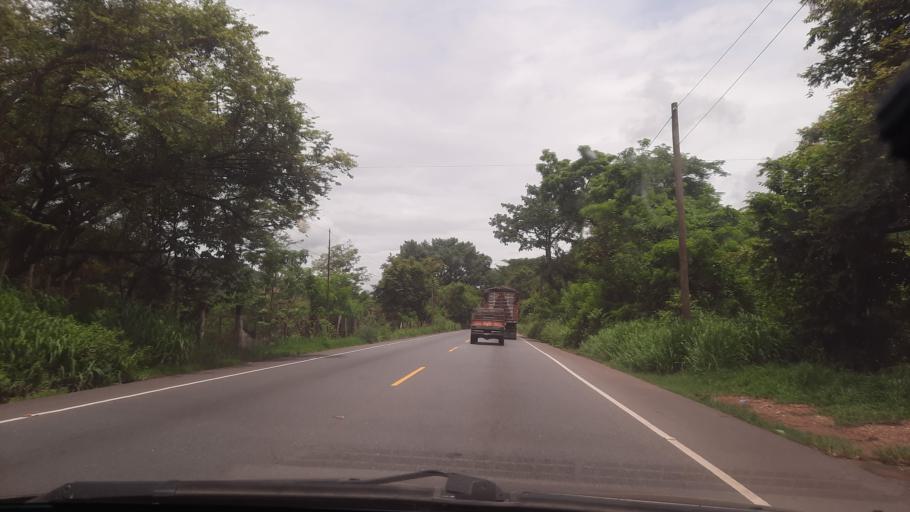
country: GT
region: Zacapa
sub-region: Municipio de Zacapa
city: Gualan
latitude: 15.2013
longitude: -89.2583
